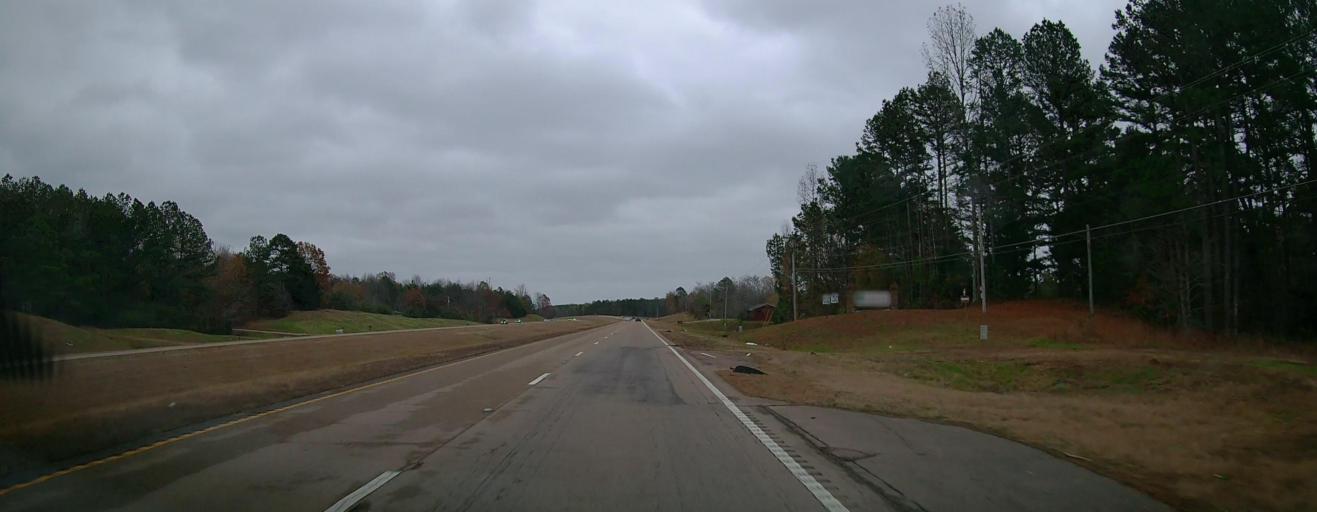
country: US
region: Mississippi
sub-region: Tippah County
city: Ripley
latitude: 34.9530
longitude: -88.9521
